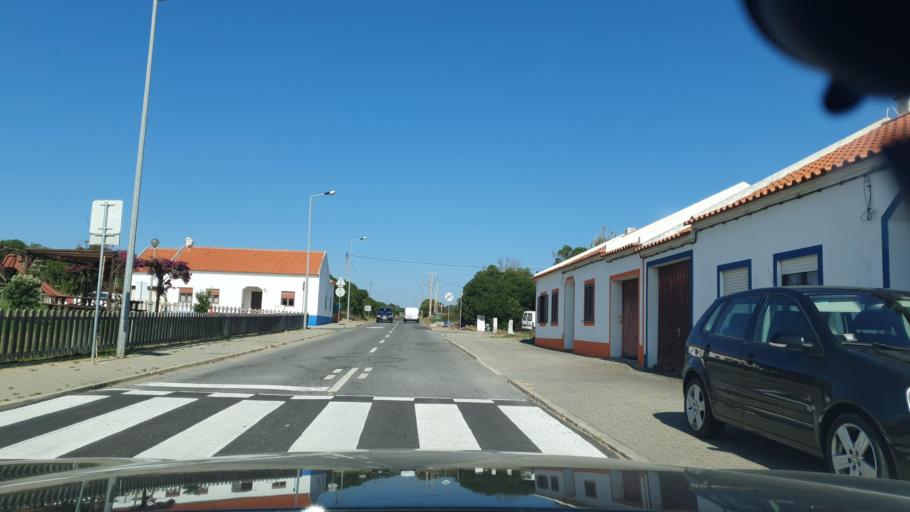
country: PT
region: Beja
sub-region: Odemira
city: Sao Teotonio
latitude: 37.4648
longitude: -8.7947
